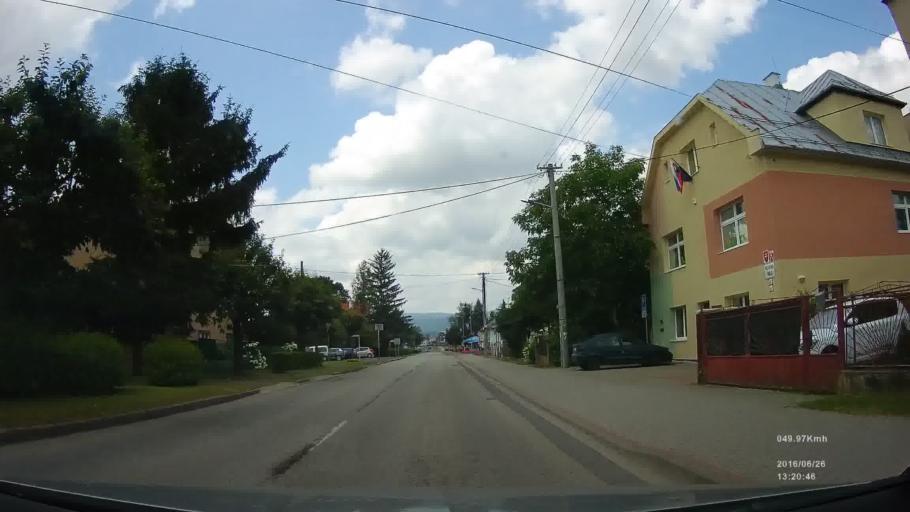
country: SK
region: Banskobystricky
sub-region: Okres Banska Bystrica
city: Zvolen
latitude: 48.6133
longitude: 19.1449
